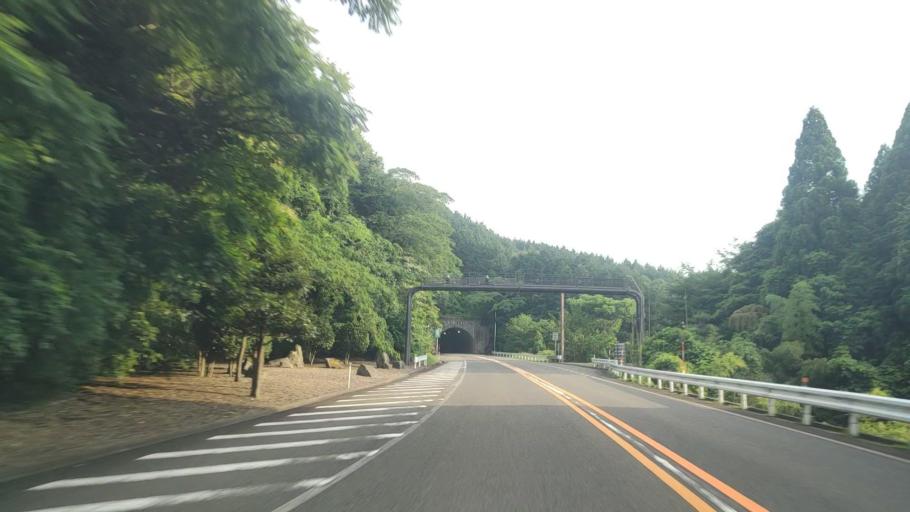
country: JP
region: Tottori
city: Kurayoshi
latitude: 35.3465
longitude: 133.7490
